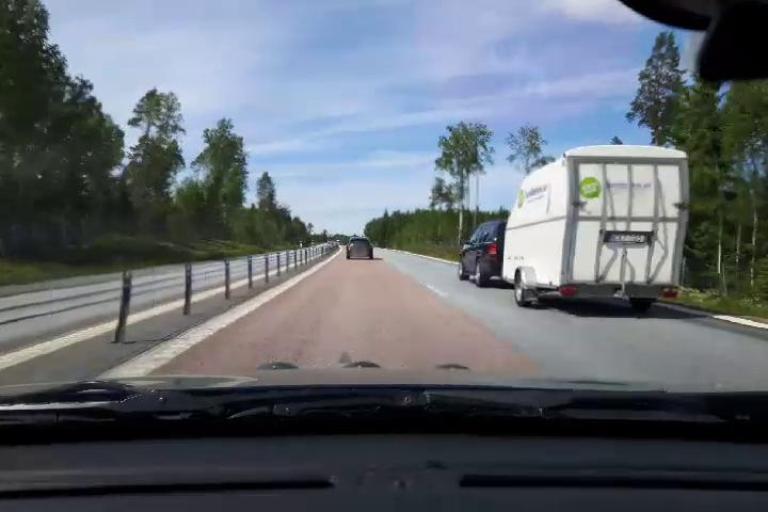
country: SE
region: Gaevleborg
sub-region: Gavle Kommun
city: Gavle
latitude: 60.7156
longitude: 17.0813
